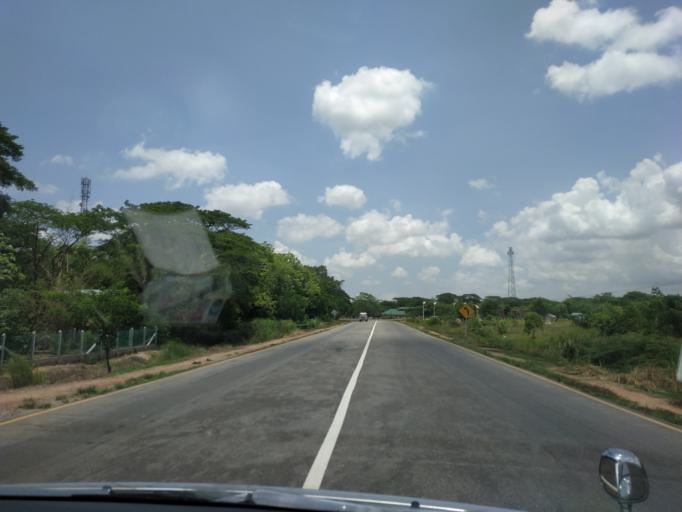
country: MM
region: Bago
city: Thanatpin
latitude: 17.4484
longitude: 96.6243
